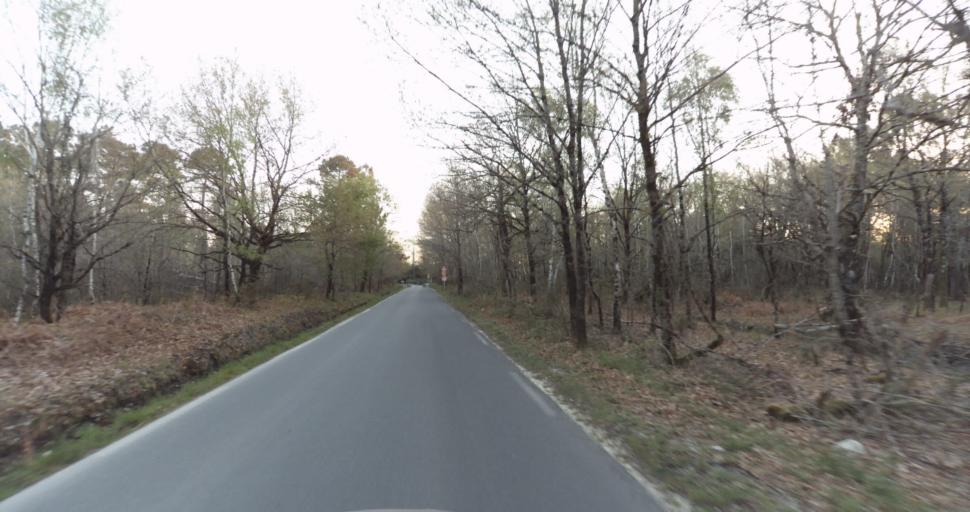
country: FR
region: Aquitaine
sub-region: Departement de la Gironde
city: Saint-Aubin-de-Medoc
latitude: 44.8047
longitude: -0.7286
